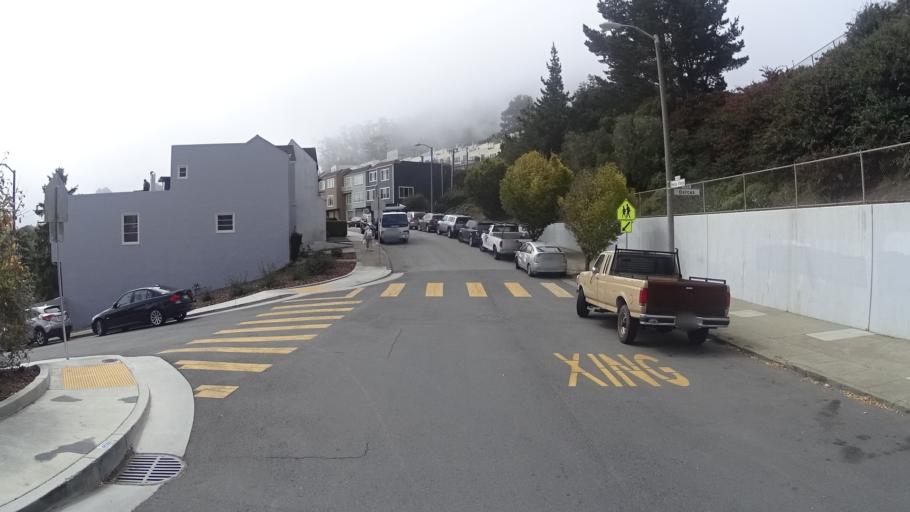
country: US
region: California
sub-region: San Mateo County
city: Daly City
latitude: 37.7380
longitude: -122.4493
